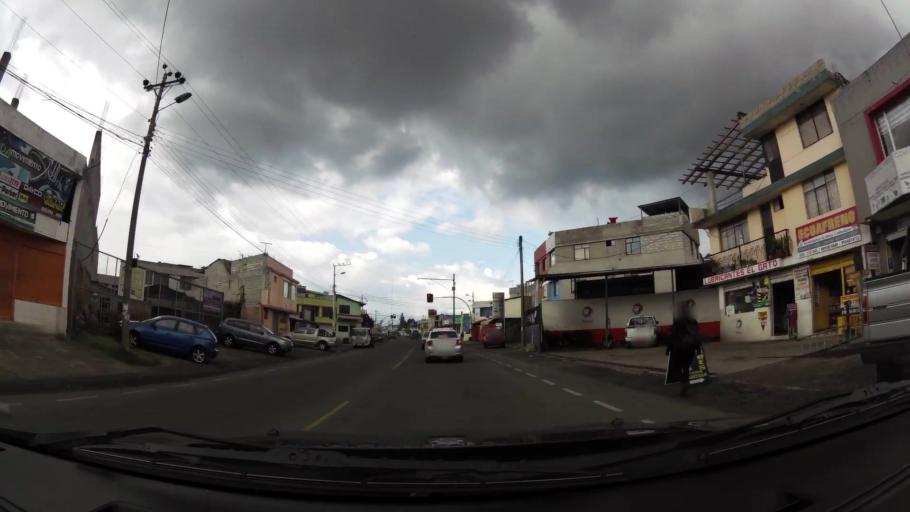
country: EC
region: Pichincha
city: Sangolqui
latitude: -0.3406
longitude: -78.4479
